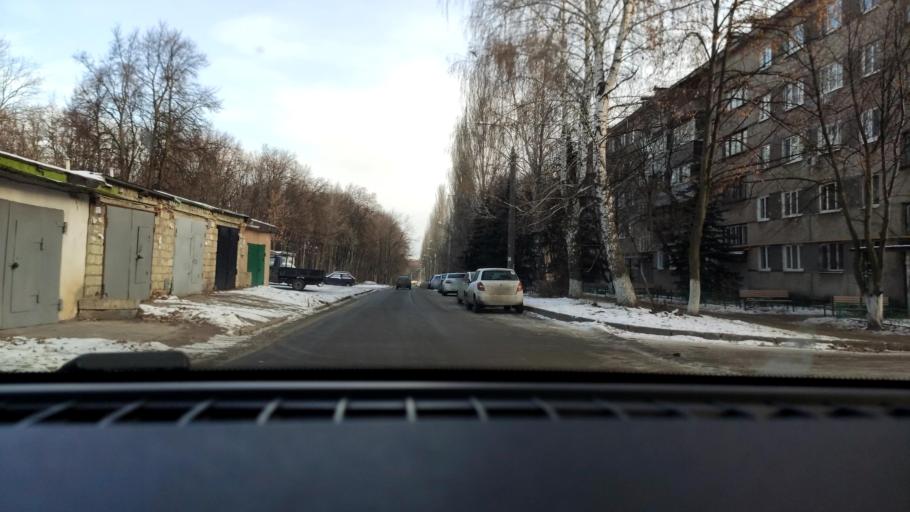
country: RU
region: Samara
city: Petra-Dubrava
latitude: 53.3050
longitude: 50.2720
